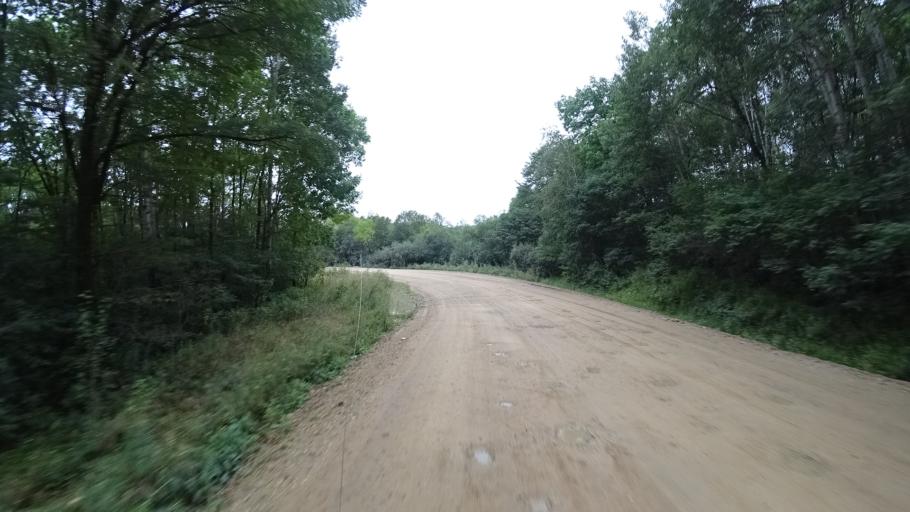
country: RU
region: Primorskiy
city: Rettikhovka
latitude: 44.1811
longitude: 132.8528
